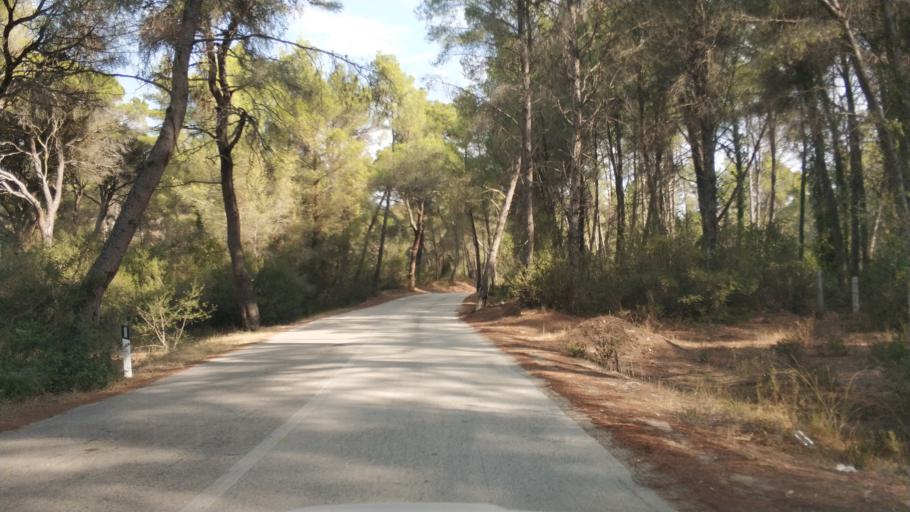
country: AL
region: Fier
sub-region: Rrethi i Lushnjes
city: Divjake
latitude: 40.9852
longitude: 19.4831
